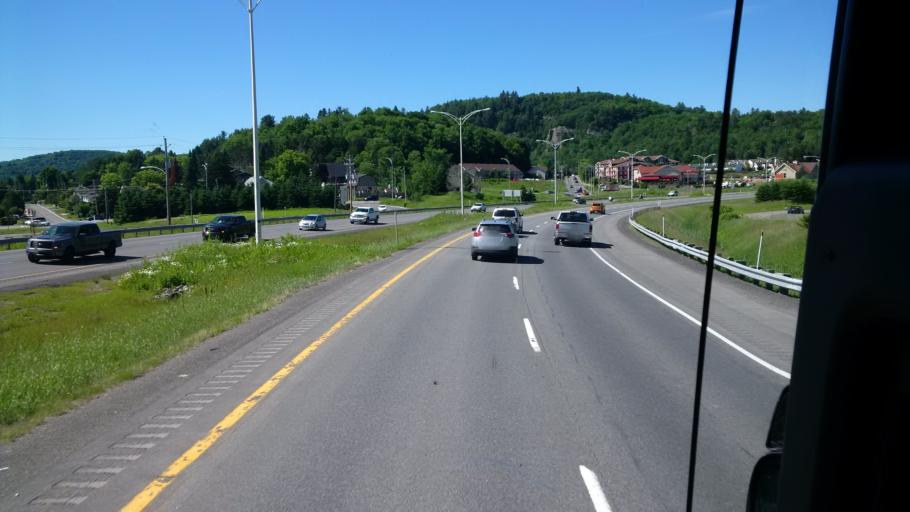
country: CA
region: Quebec
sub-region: Laurentides
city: Saint-Sauveur
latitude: 45.8927
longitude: -74.1470
